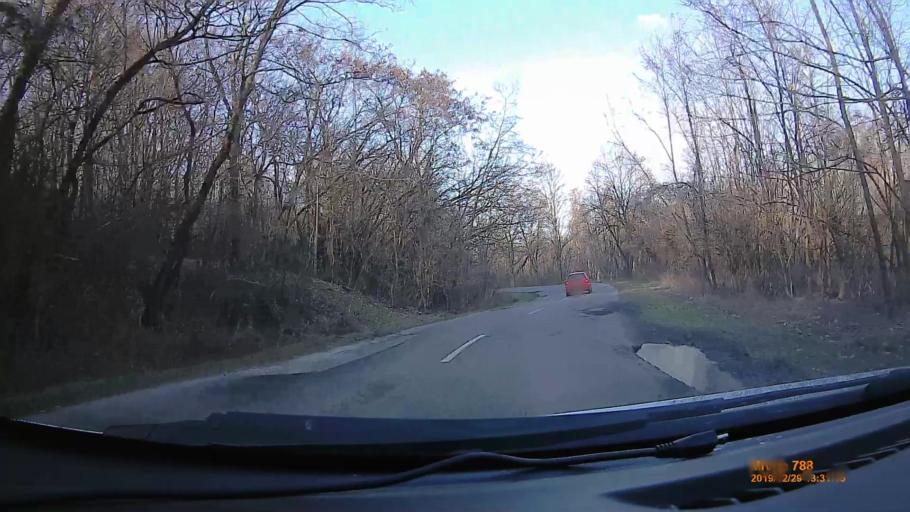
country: HU
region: Heves
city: Verpelet
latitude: 47.8809
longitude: 20.1950
